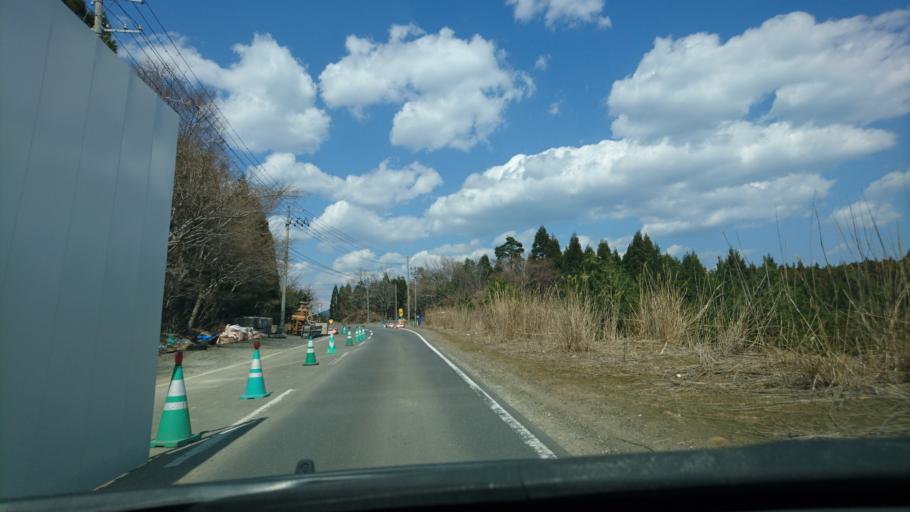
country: JP
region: Miyagi
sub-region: Oshika Gun
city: Onagawa Cho
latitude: 38.4771
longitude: 141.4935
